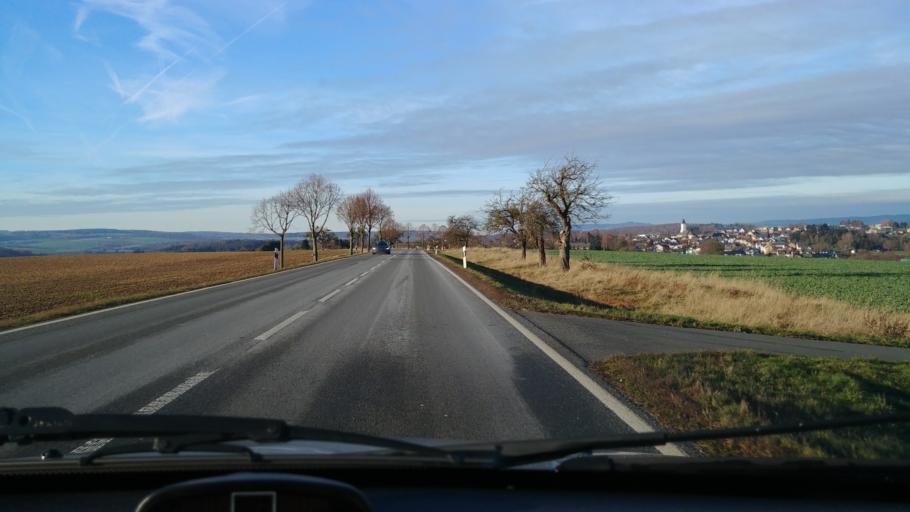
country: DE
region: Rheinland-Pfalz
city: Hunzel
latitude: 50.2650
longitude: 7.8447
